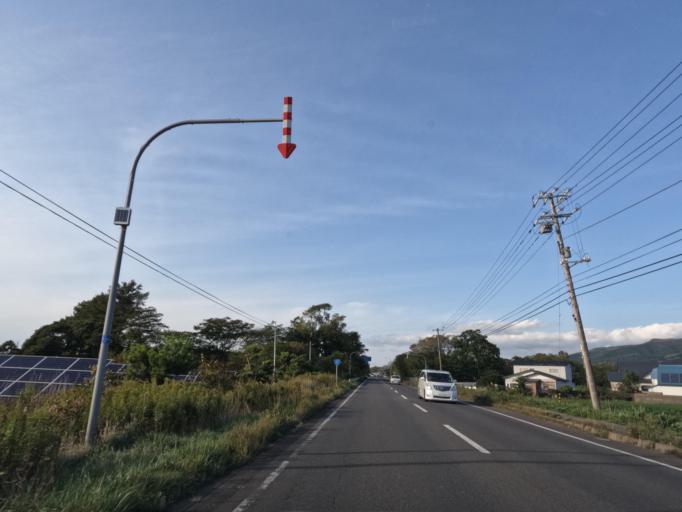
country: JP
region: Hokkaido
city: Date
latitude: 42.4434
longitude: 140.8985
